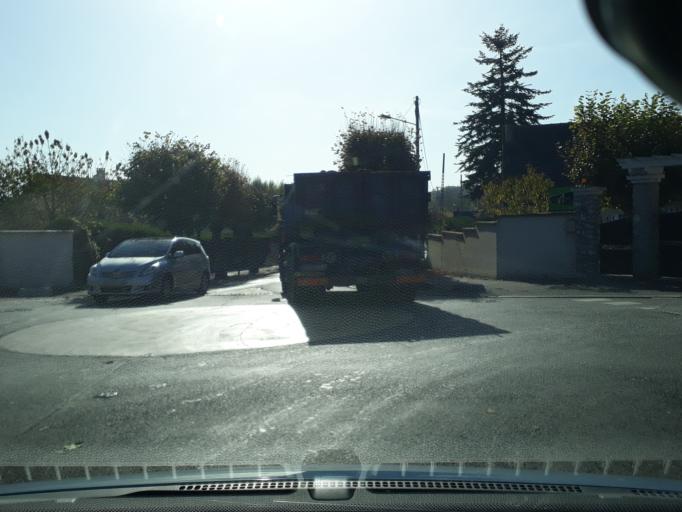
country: FR
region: Ile-de-France
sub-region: Departement de Seine-et-Marne
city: Chartrettes
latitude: 48.4860
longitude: 2.6967
